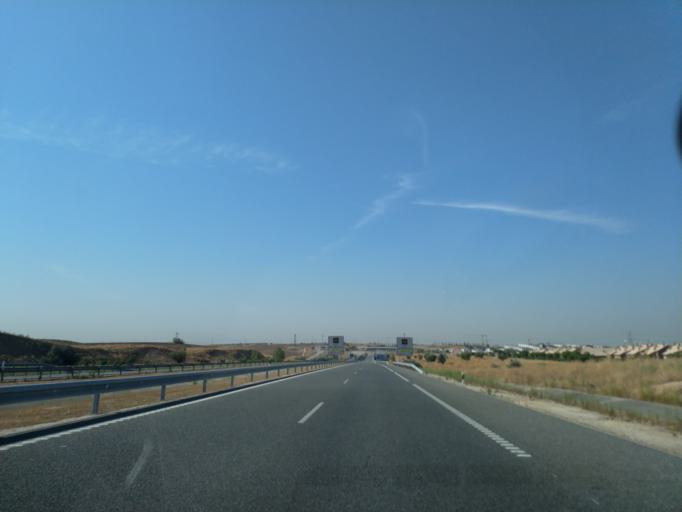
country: ES
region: Madrid
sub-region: Provincia de Madrid
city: Arroyomolinos
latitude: 40.2659
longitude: -3.8998
